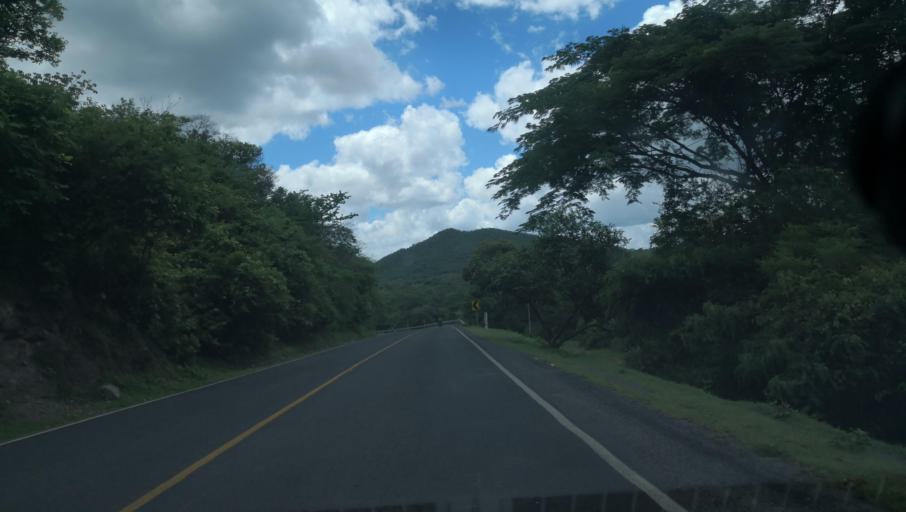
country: NI
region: Madriz
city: Palacaguina
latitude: 13.4486
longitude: -86.4430
